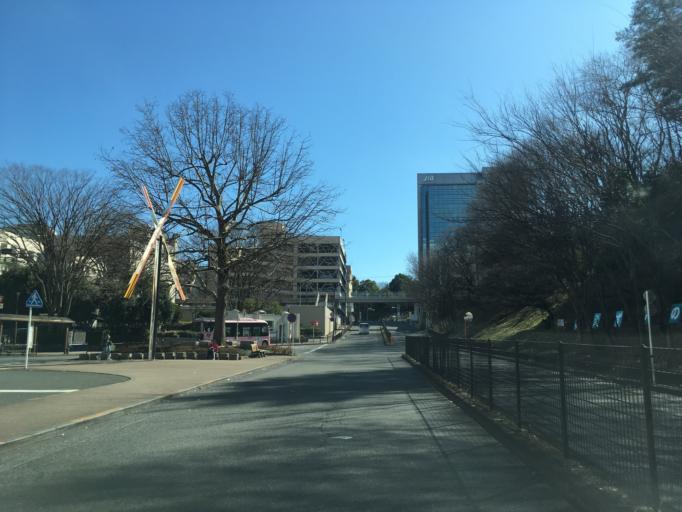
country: JP
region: Tokyo
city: Hino
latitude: 35.6301
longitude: 139.4473
